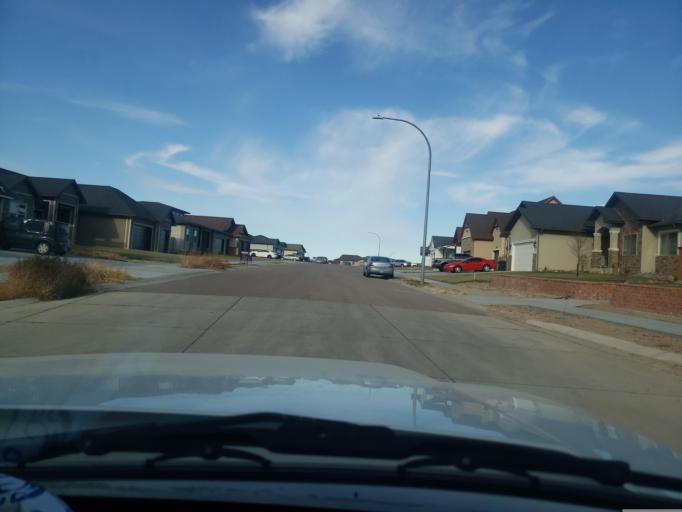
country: US
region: Kansas
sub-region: Finney County
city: Garden City
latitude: 37.9841
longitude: -100.8249
